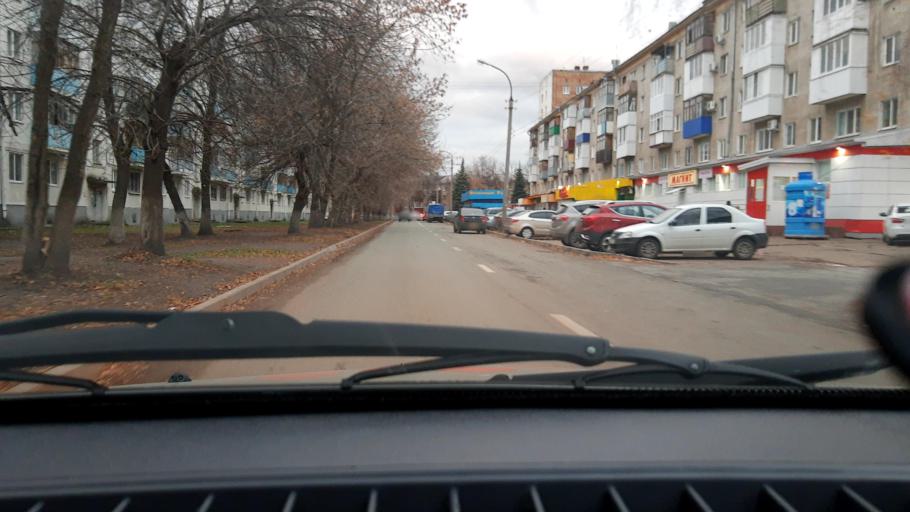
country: RU
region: Bashkortostan
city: Ufa
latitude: 54.8178
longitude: 56.1100
